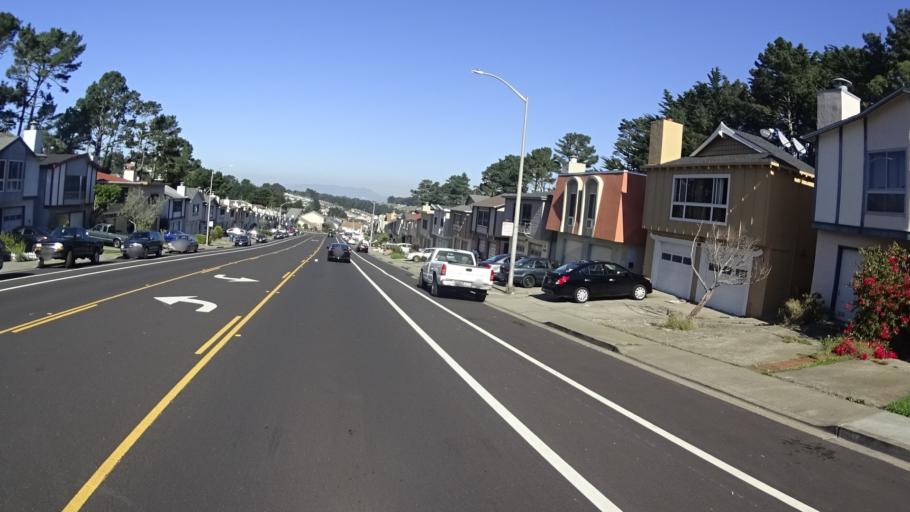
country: US
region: California
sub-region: San Mateo County
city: Colma
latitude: 37.6554
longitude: -122.4695
